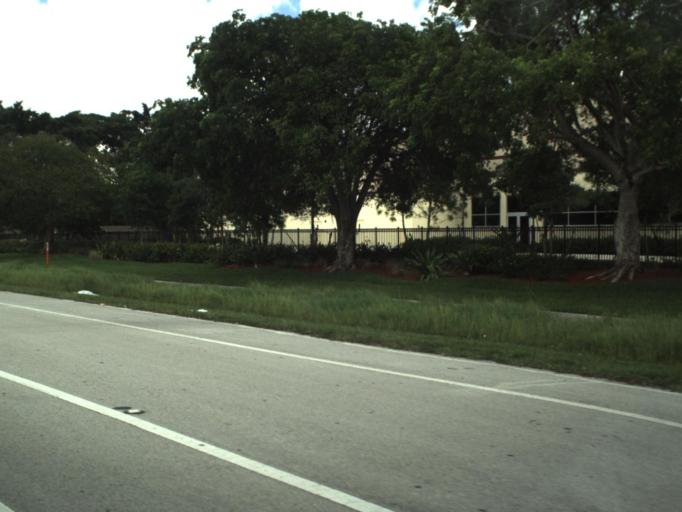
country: US
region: Florida
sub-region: Broward County
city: Cooper City
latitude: 26.0082
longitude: -80.2858
